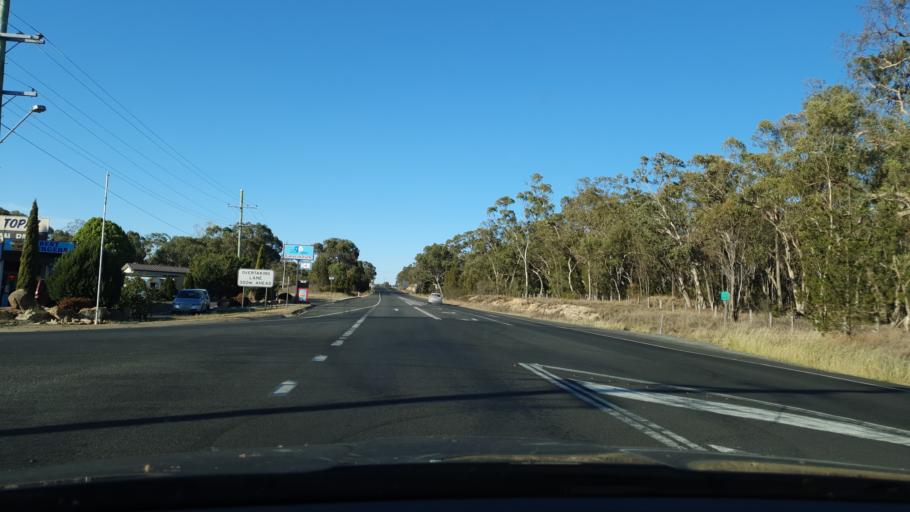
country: AU
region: Queensland
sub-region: Southern Downs
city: Stanthorpe
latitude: -28.6981
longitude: 151.9060
